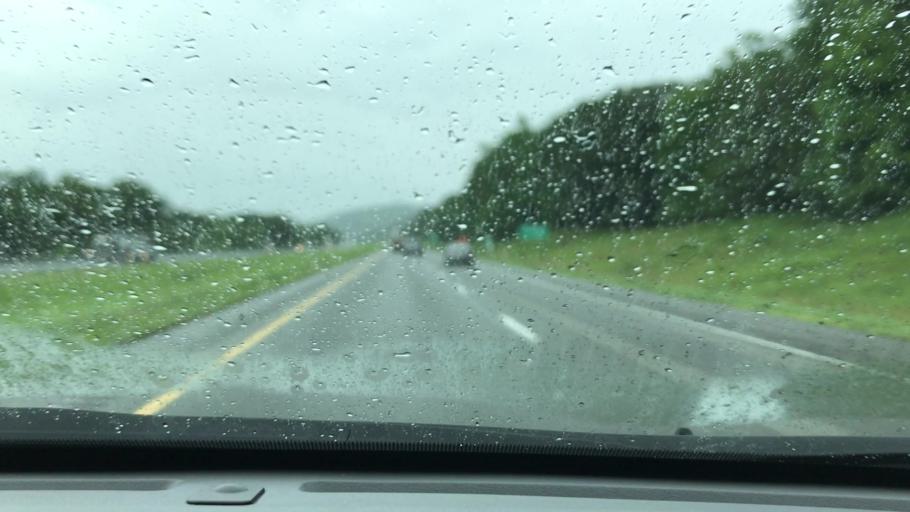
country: US
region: Pennsylvania
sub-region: Blair County
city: Tyrone
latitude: 40.6509
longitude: -78.2587
